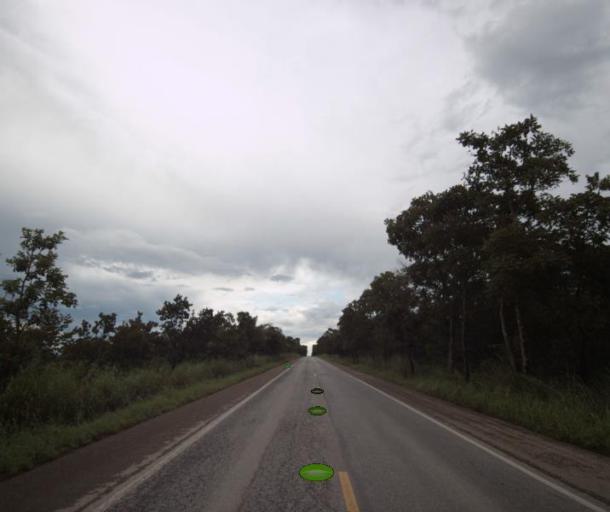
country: BR
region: Goias
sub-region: Porangatu
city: Porangatu
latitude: -13.6547
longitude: -49.0368
